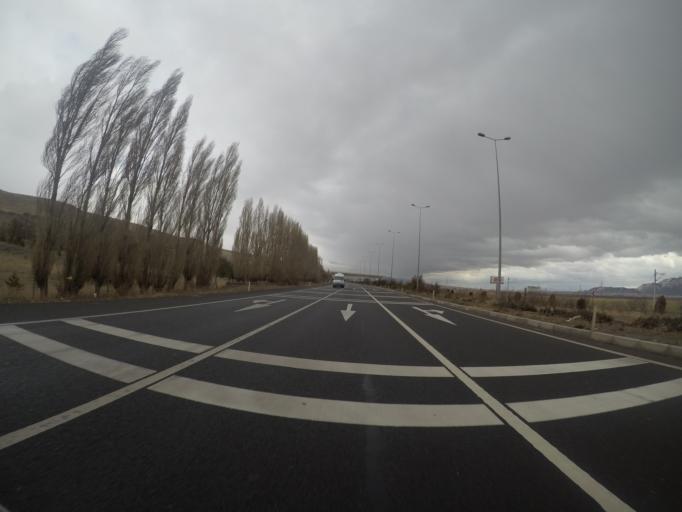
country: TR
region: Kayseri
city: Incesu
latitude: 38.7238
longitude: 35.2758
